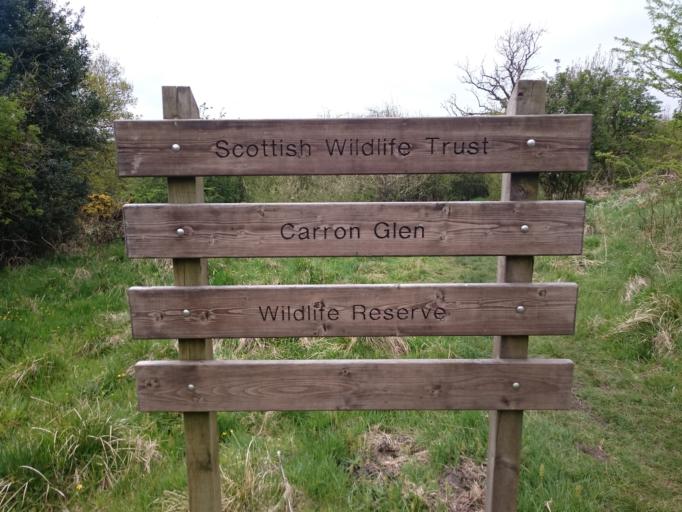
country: GB
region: Scotland
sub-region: Falkirk
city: Dunipace
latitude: 56.0267
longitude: -3.9357
